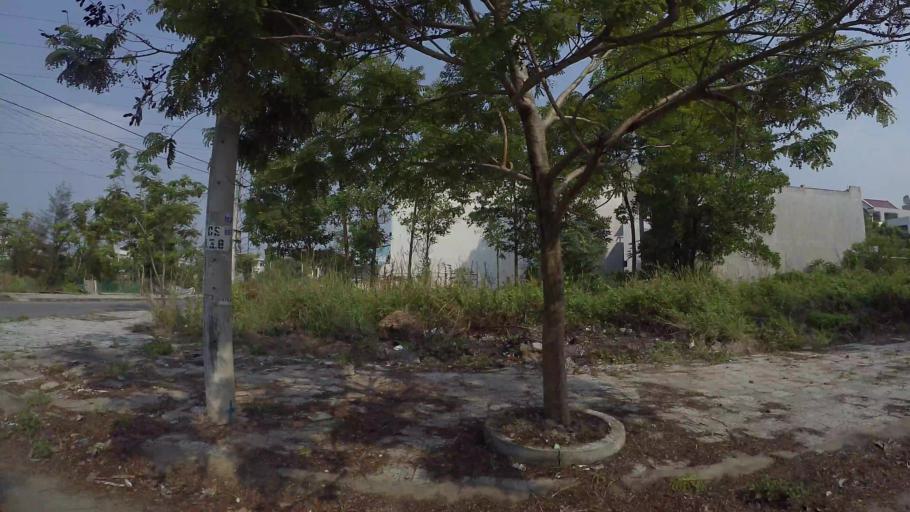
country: VN
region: Da Nang
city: Ngu Hanh Son
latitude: 16.0266
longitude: 108.2425
